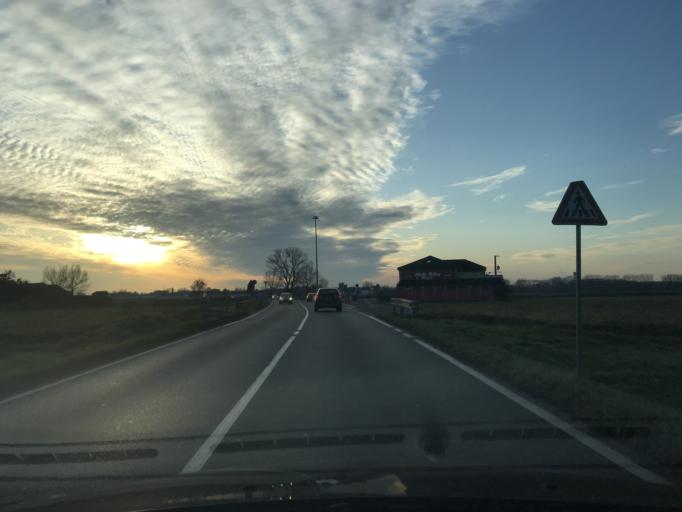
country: IT
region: Lombardy
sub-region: Provincia di Lodi
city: Castiraga Vidardo
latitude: 45.2502
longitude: 9.4242
